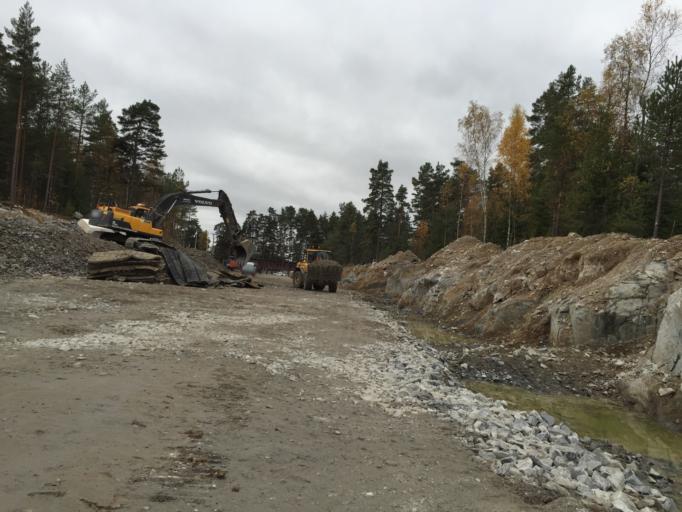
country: SE
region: Vaestmanland
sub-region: Hallstahammars Kommun
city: Hallstahammar
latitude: 59.6247
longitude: 16.2114
